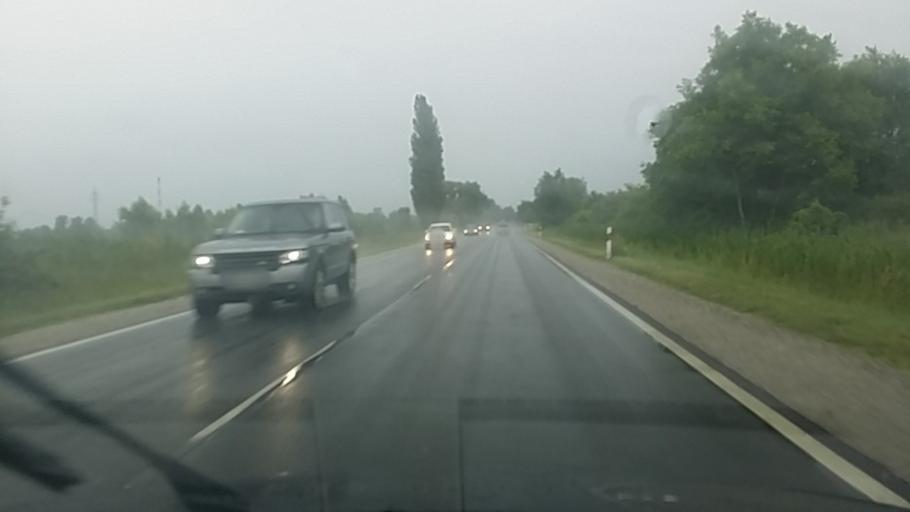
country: HU
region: Hajdu-Bihar
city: Hajduhadhaz
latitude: 47.6982
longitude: 21.6568
